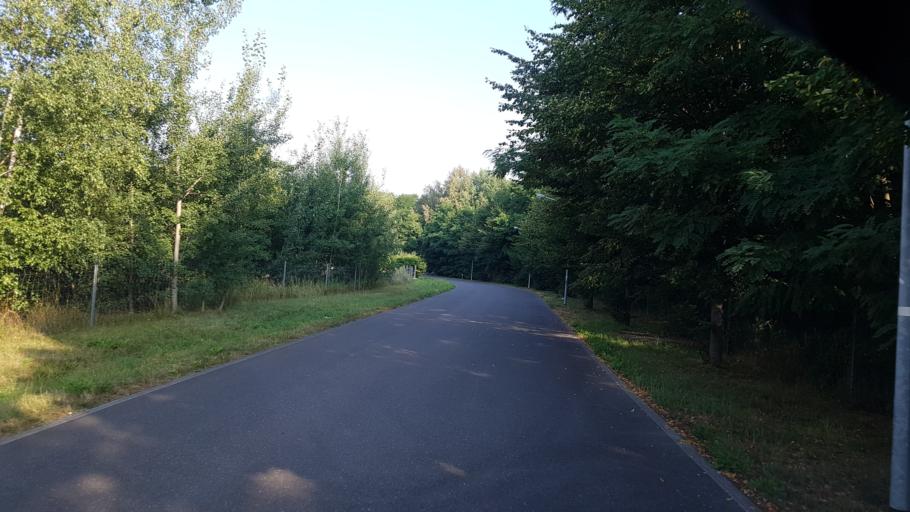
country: DE
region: Brandenburg
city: Grossraschen
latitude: 51.5827
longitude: 13.9817
